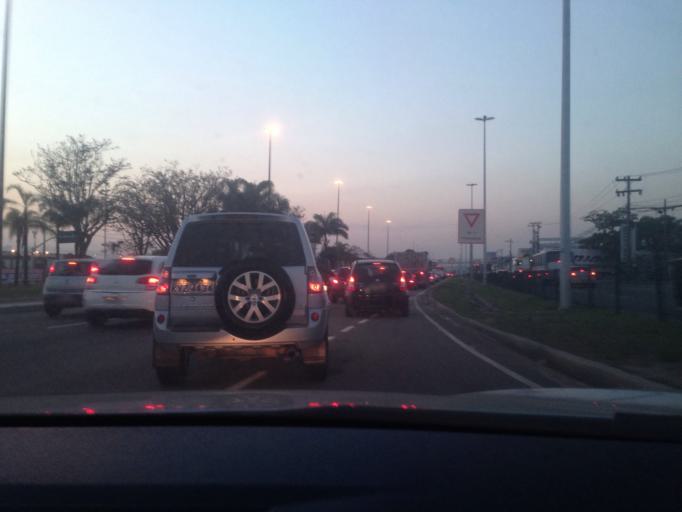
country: BR
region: Rio de Janeiro
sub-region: Rio De Janeiro
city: Rio de Janeiro
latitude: -22.9920
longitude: -43.3655
